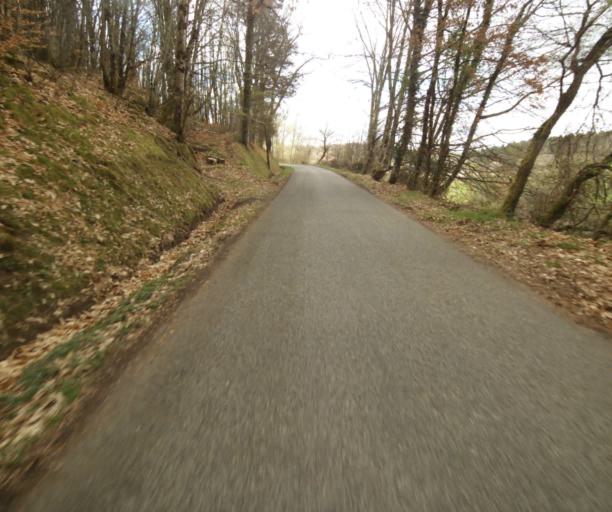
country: FR
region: Limousin
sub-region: Departement de la Correze
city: Laguenne
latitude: 45.2431
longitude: 1.8898
